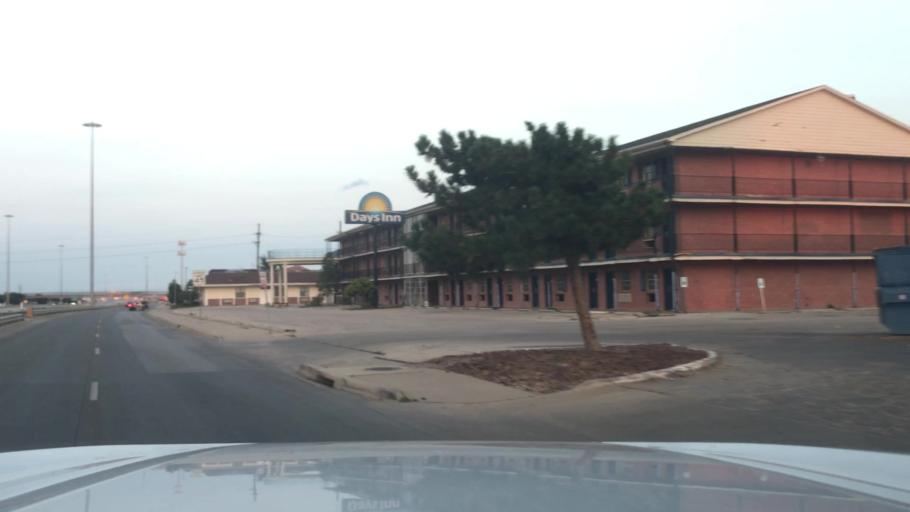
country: US
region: Texas
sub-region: Lubbock County
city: Lubbock
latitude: 33.5923
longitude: -101.8701
